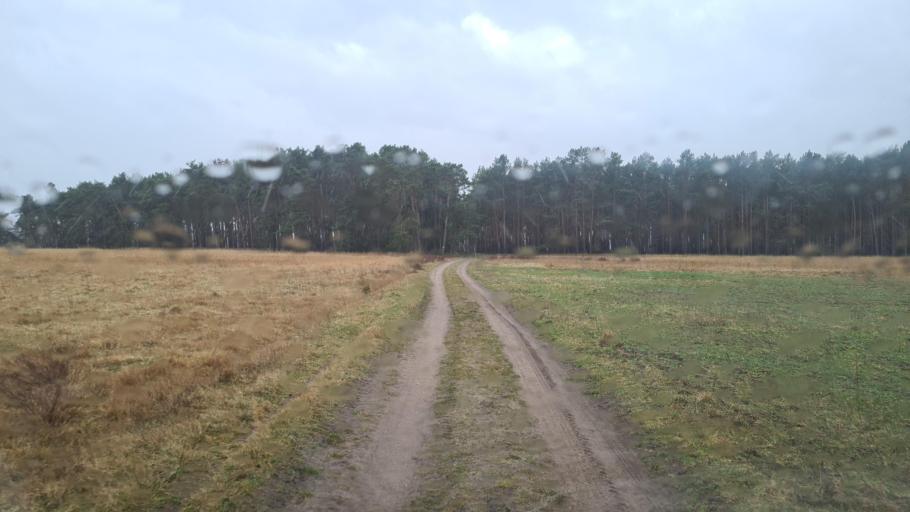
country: DE
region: Brandenburg
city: Bruck
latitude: 52.1606
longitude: 12.7204
